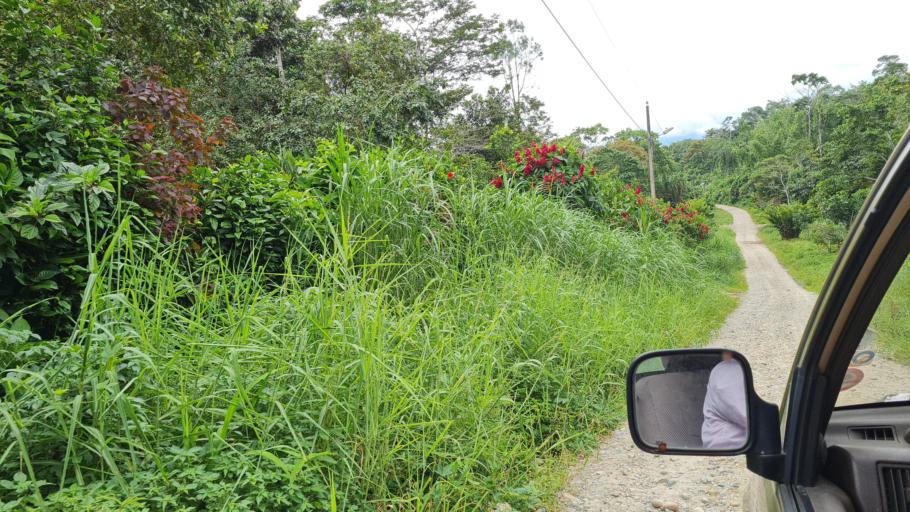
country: EC
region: Napo
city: Tena
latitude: -0.9995
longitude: -77.7569
